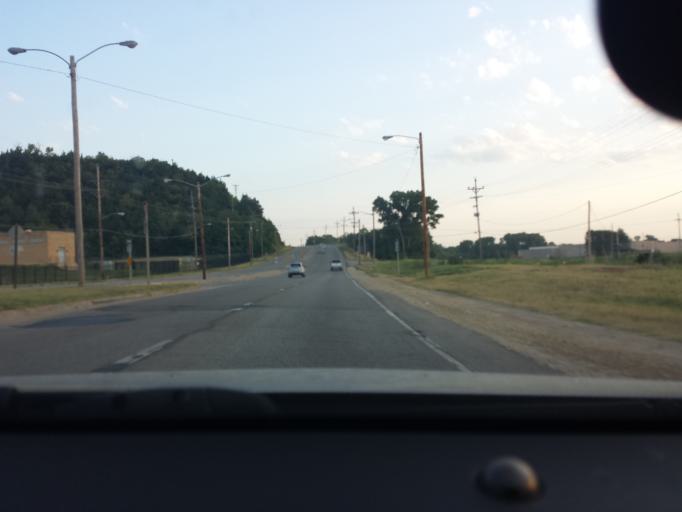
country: US
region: Kansas
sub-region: Riley County
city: Manhattan
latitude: 39.1908
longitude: -96.5602
